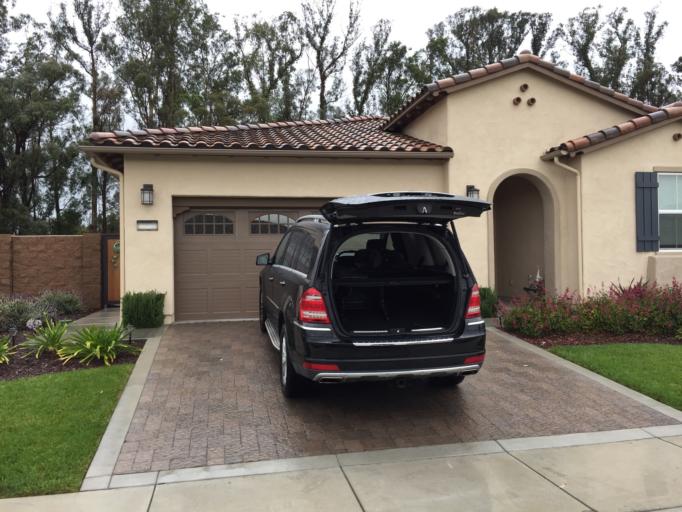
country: US
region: California
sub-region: San Luis Obispo County
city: Callender
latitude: 35.0344
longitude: -120.5471
